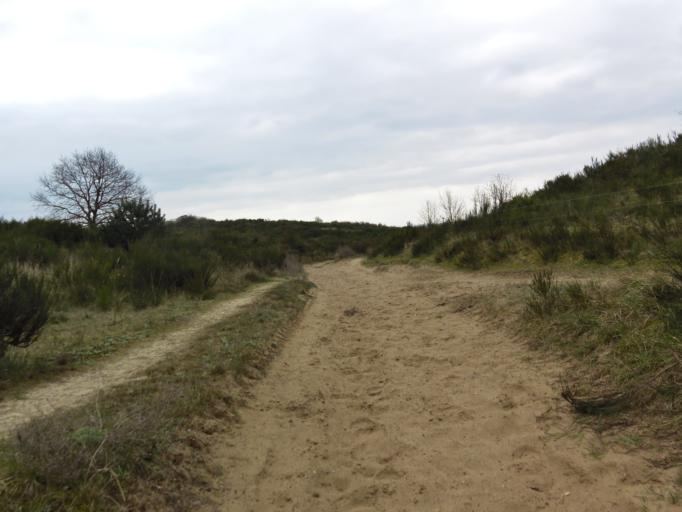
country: DE
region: Mecklenburg-Vorpommern
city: Hiddensee
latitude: 54.5953
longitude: 13.1207
